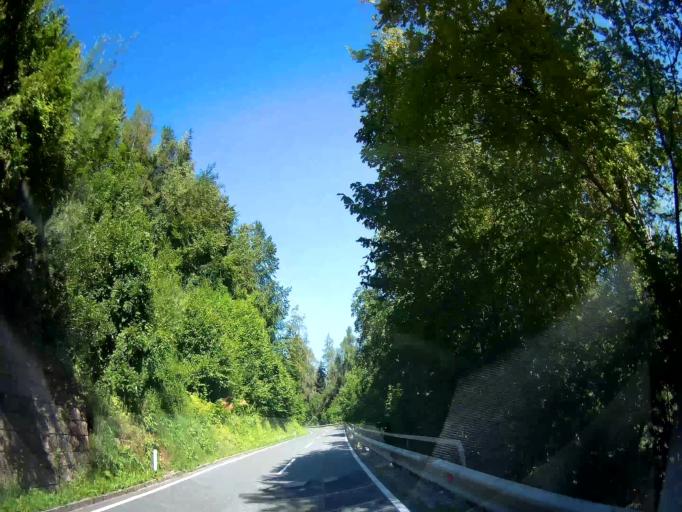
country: AT
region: Carinthia
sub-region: Politischer Bezirk Volkermarkt
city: Gallizien
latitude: 46.5555
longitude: 14.4875
